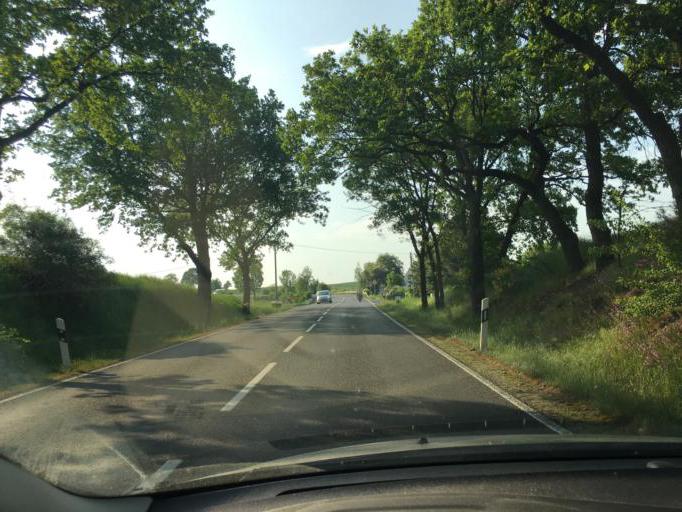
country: DE
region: Saxony
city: Colditz
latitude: 51.1431
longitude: 12.7763
